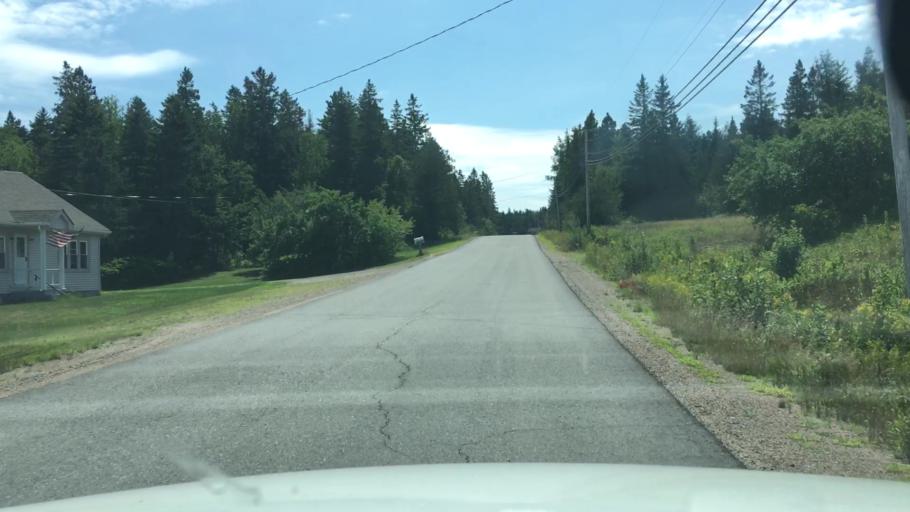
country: CA
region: New Brunswick
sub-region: Charlotte County
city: Saint Andrews
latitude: 44.9905
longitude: -67.0673
